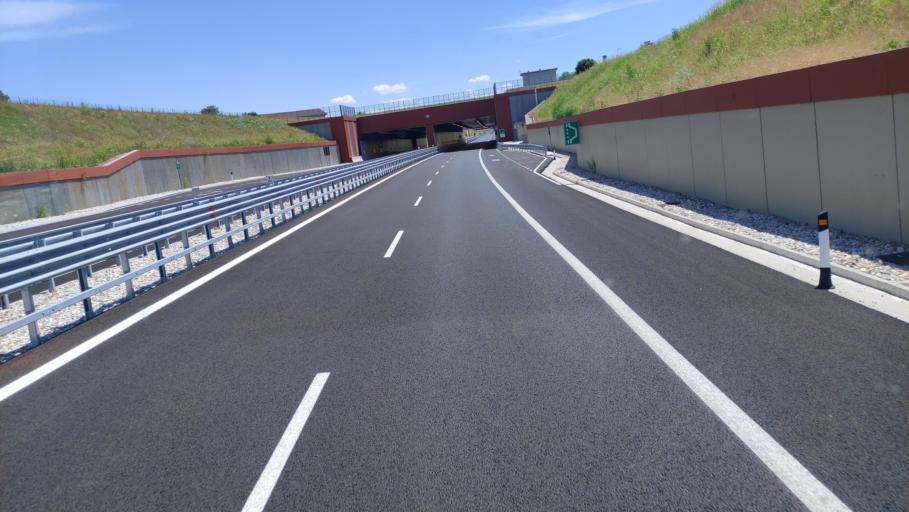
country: IT
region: Veneto
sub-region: Provincia di Treviso
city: San Vito
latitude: 45.7433
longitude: 11.9317
